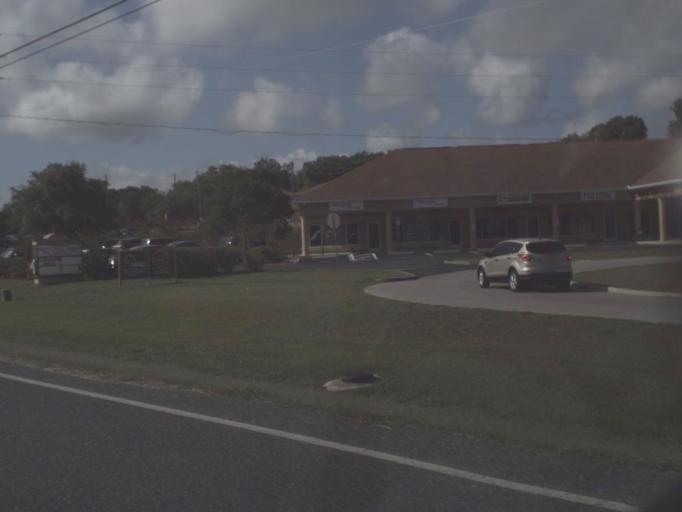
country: US
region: Florida
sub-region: Lake County
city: Lady Lake
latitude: 28.9009
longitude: -81.9127
